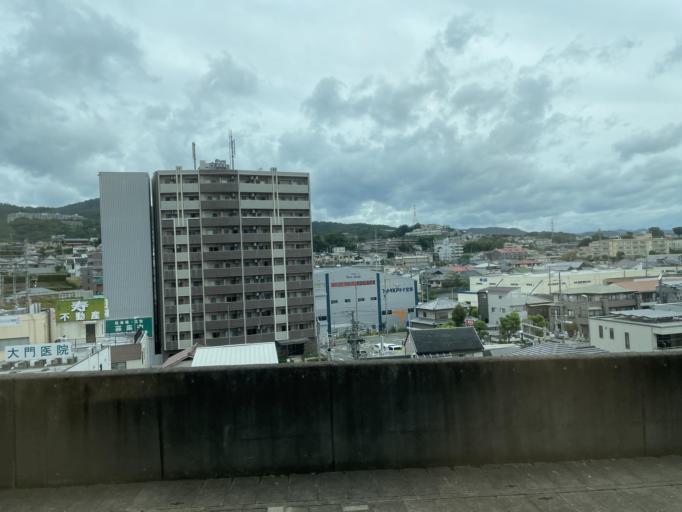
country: JP
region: Hyogo
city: Takarazuka
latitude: 34.8091
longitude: 135.3446
